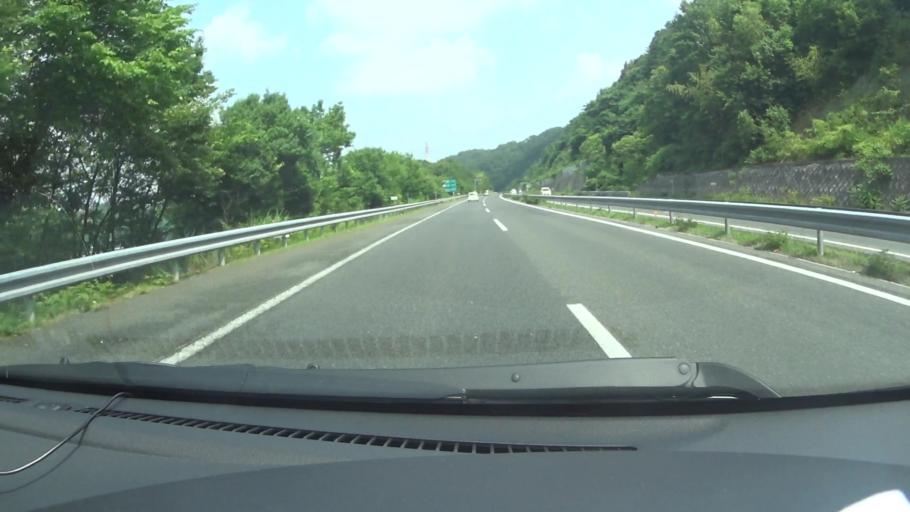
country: JP
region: Kyoto
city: Kameoka
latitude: 35.0957
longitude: 135.4980
